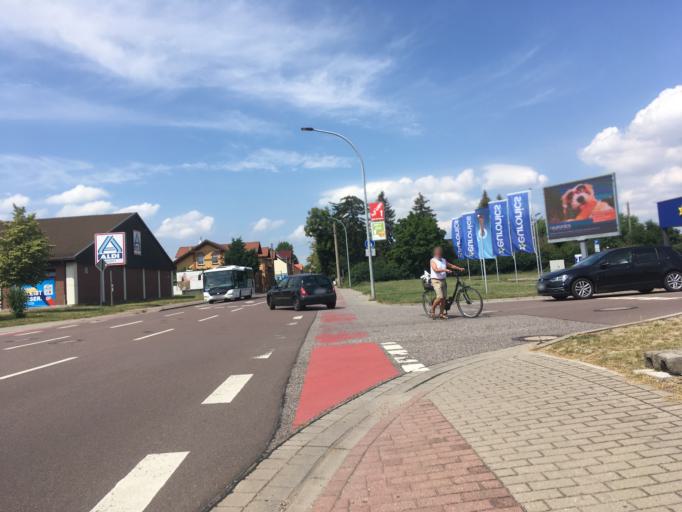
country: DE
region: Saxony-Anhalt
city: Koethen
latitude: 51.7544
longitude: 12.0001
